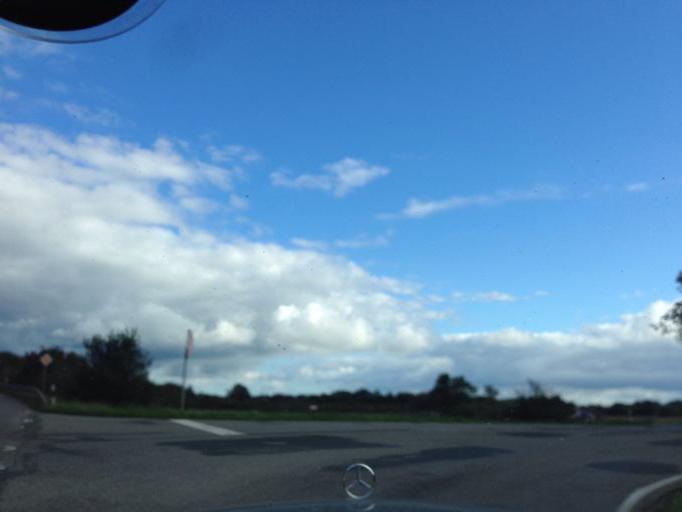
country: DE
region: Schleswig-Holstein
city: Niebull
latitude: 54.7788
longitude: 8.8374
